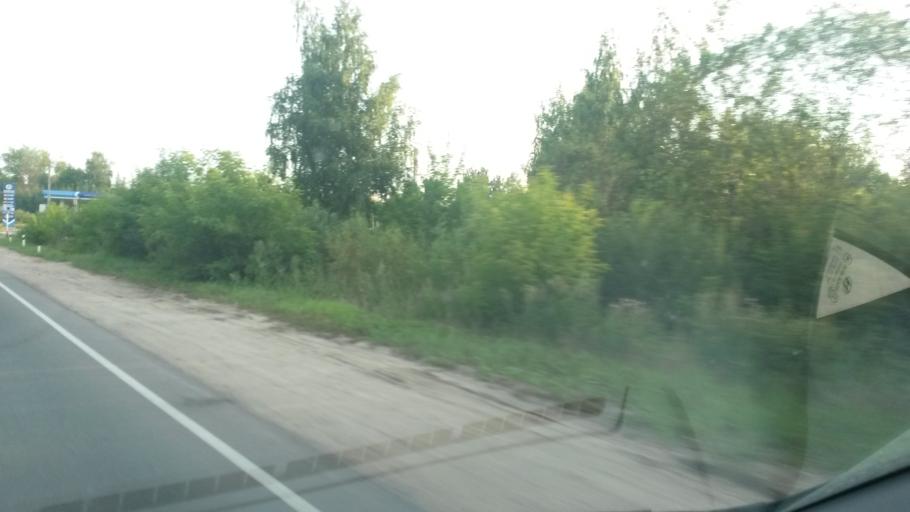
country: RU
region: Ivanovo
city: Novo-Talitsy
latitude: 57.0073
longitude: 40.8756
